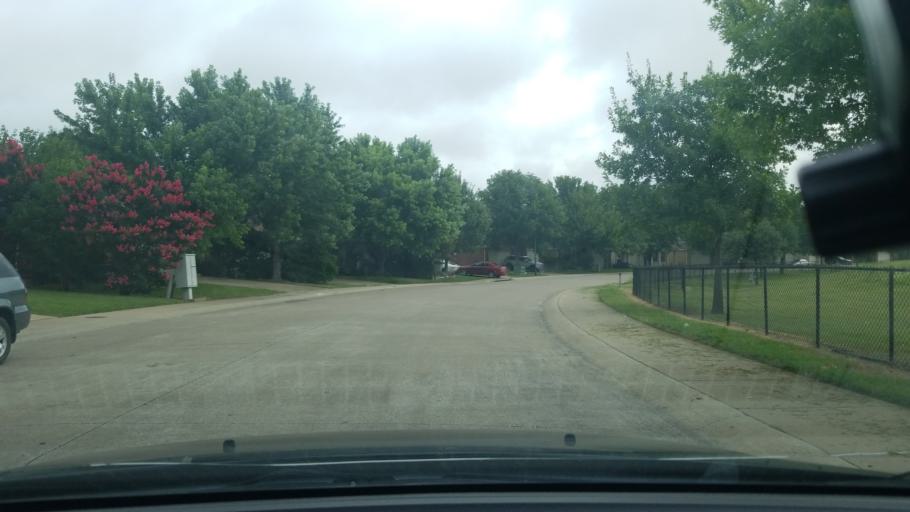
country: US
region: Texas
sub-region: Dallas County
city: Balch Springs
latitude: 32.7846
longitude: -96.6936
